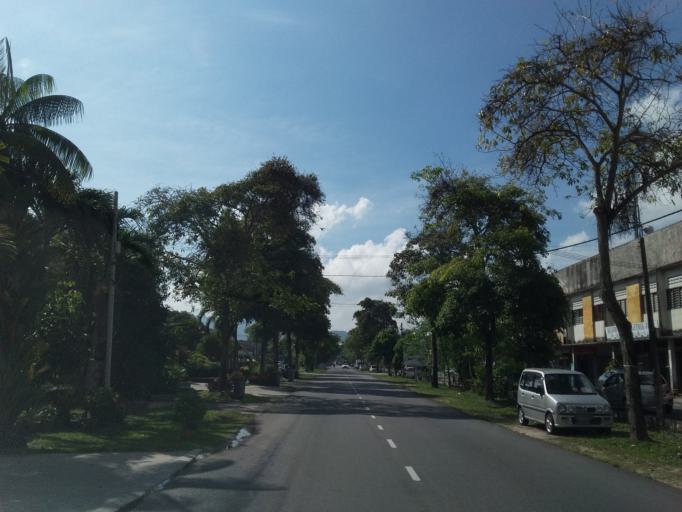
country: MY
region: Johor
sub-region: Daerah Batu Pahat
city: Batu Pahat
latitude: 1.8422
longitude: 102.9274
